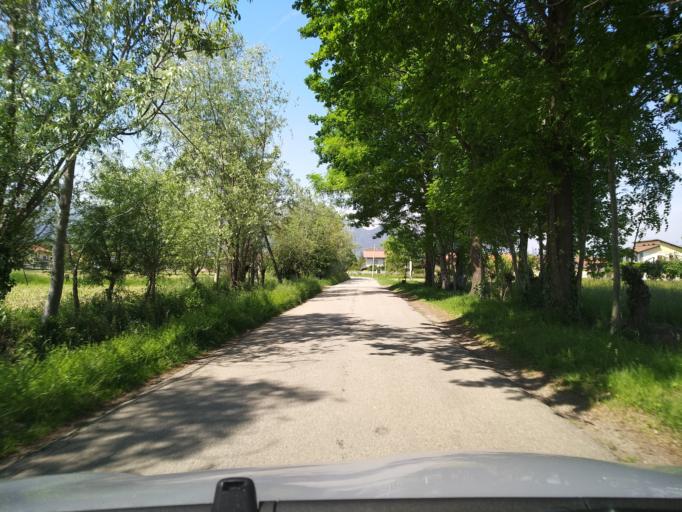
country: IT
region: Piedmont
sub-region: Provincia di Torino
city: Frossasco
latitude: 44.9014
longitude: 7.3560
